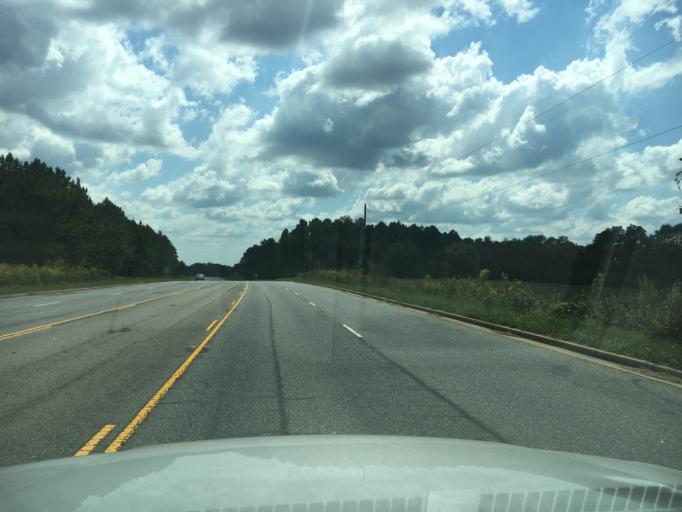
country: US
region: South Carolina
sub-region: Greenwood County
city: Ware Shoals
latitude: 34.4949
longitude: -82.2868
